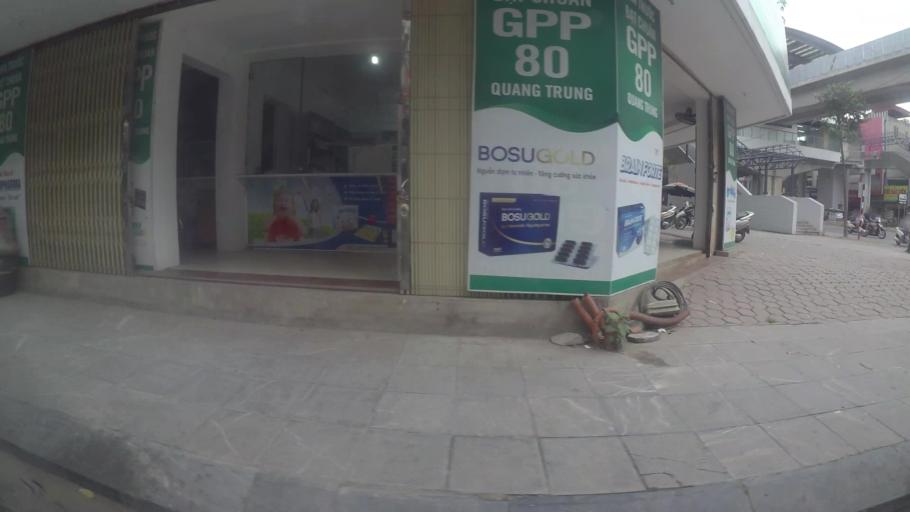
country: VN
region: Ha Noi
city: Ha Dong
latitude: 20.9699
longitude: 105.7742
